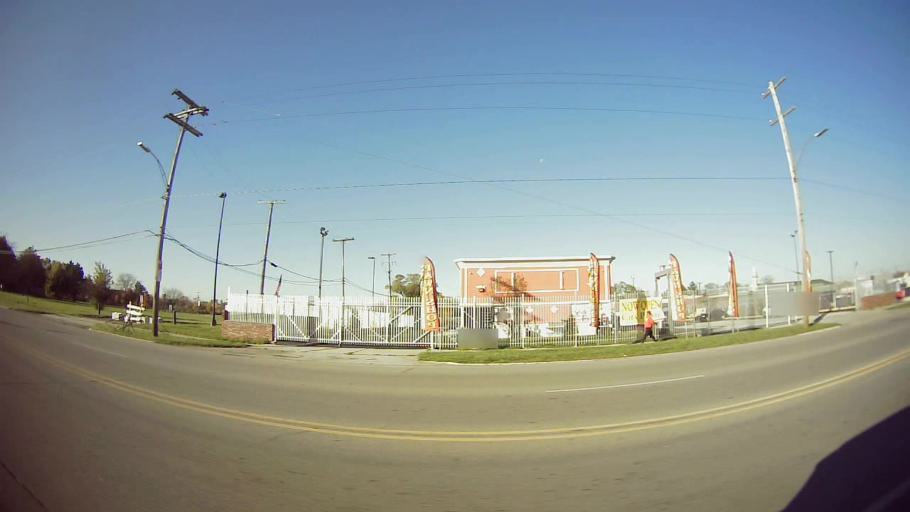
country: US
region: Michigan
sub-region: Wayne County
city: Dearborn
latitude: 42.3566
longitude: -83.1968
